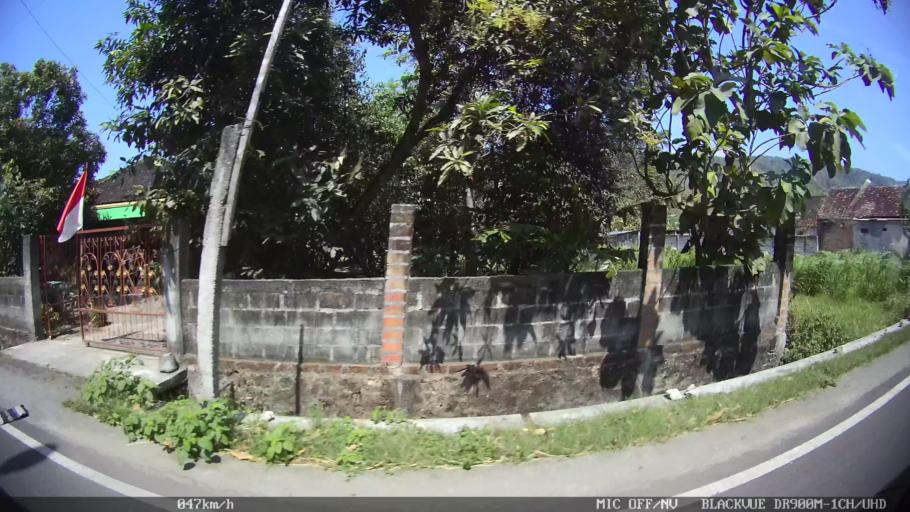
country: ID
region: Daerah Istimewa Yogyakarta
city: Pundong
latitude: -7.9681
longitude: 110.3528
